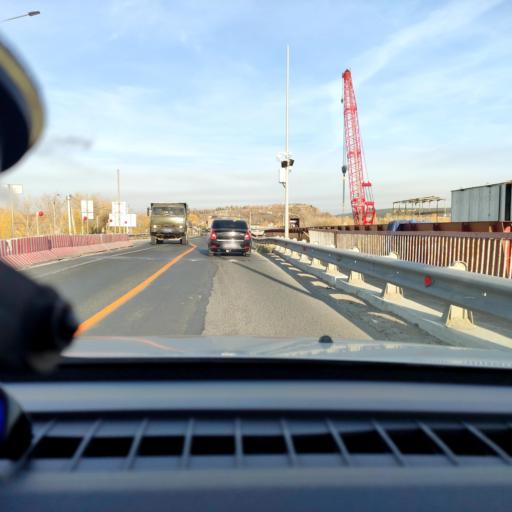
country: RU
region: Samara
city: Volzhskiy
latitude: 53.4129
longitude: 50.1360
